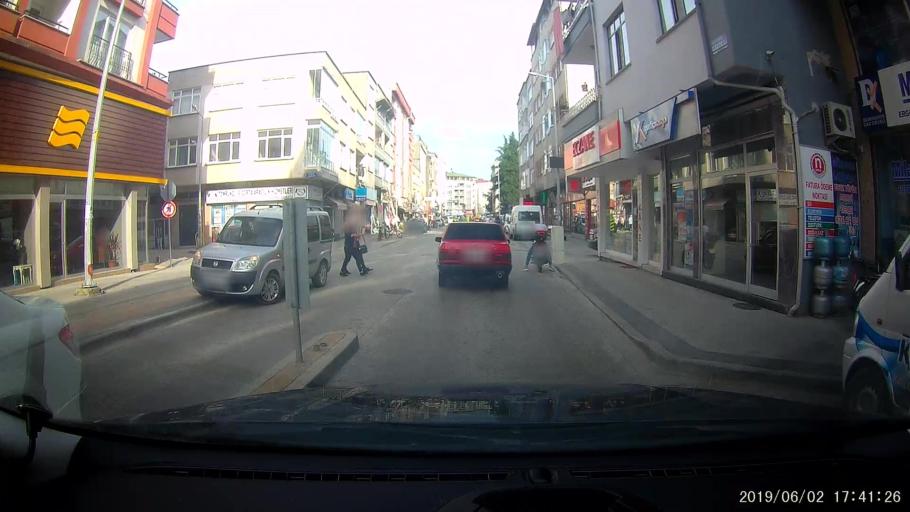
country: TR
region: Samsun
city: Terme
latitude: 41.2102
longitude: 36.9698
